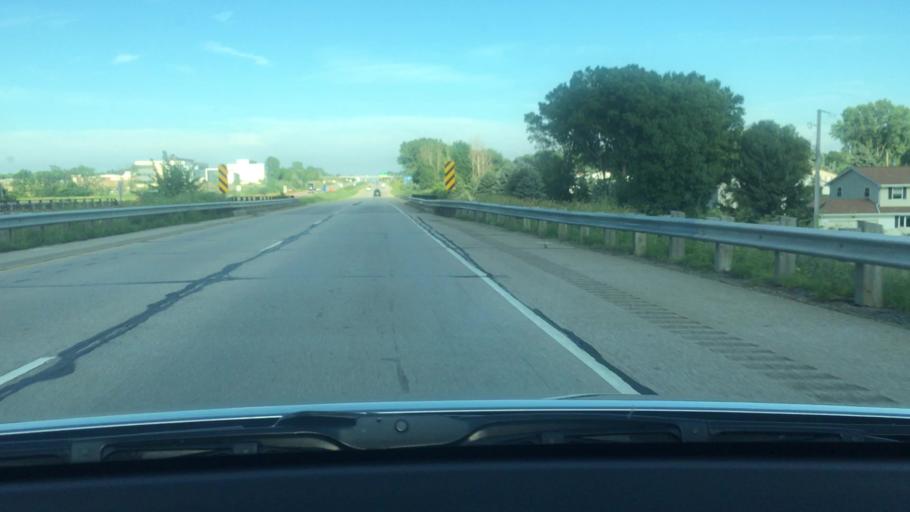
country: US
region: Wisconsin
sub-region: Outagamie County
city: Appleton
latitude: 44.2988
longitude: -88.4314
